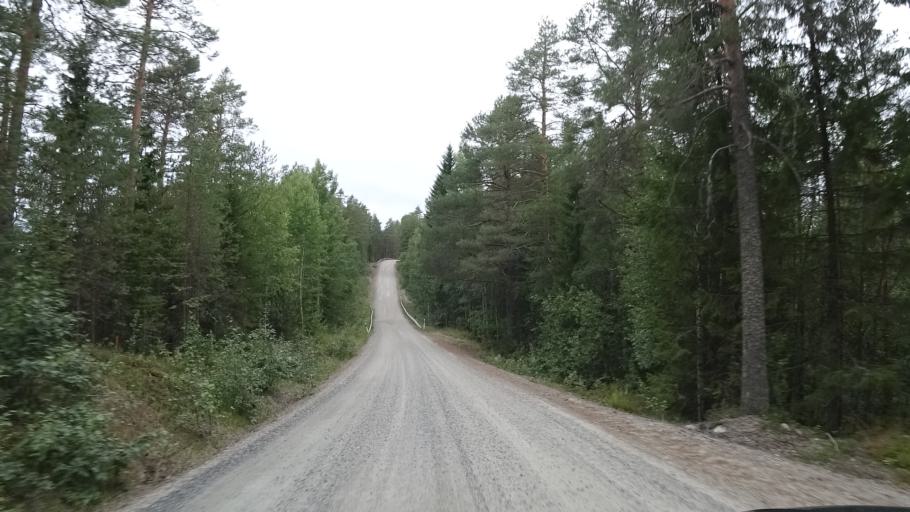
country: FI
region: North Karelia
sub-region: Pielisen Karjala
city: Lieksa
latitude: 63.2321
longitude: 30.3713
